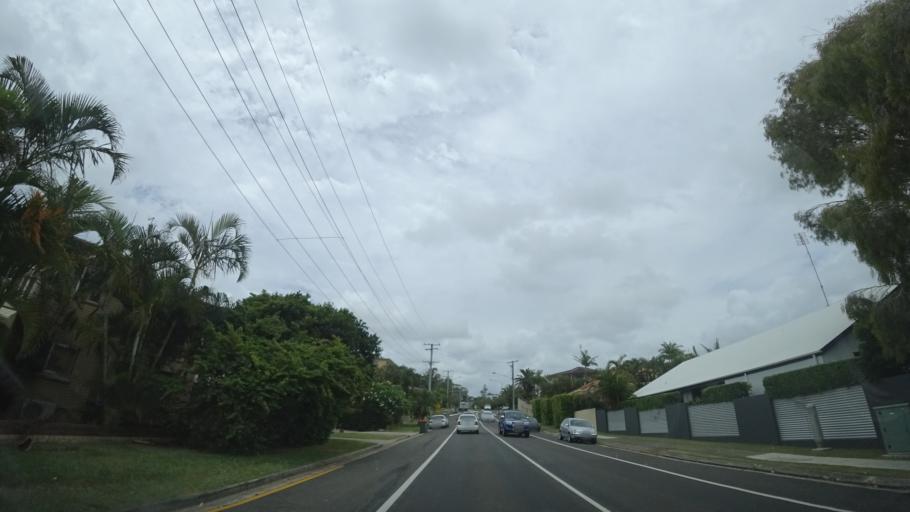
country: AU
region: Queensland
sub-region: Sunshine Coast
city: Mooloolaba
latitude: -26.6713
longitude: 153.1068
